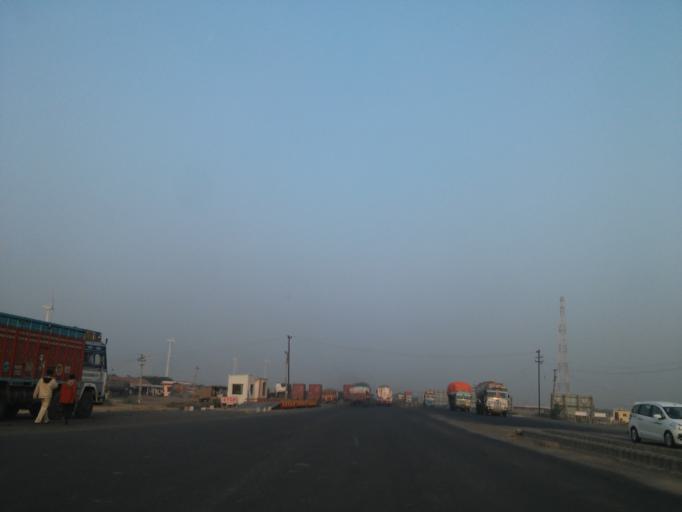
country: IN
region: Gujarat
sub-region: Kachchh
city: Rapar
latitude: 23.2340
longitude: 70.6890
